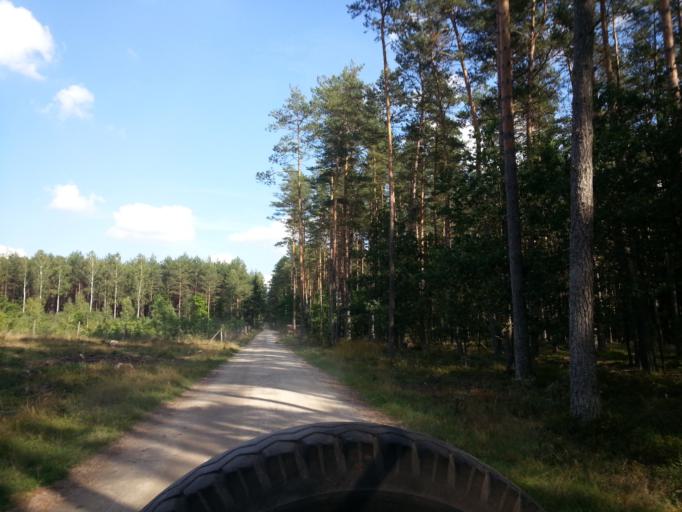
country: PL
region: Kujawsko-Pomorskie
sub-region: Powiat brodnicki
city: Gorzno
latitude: 53.1803
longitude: 19.7238
